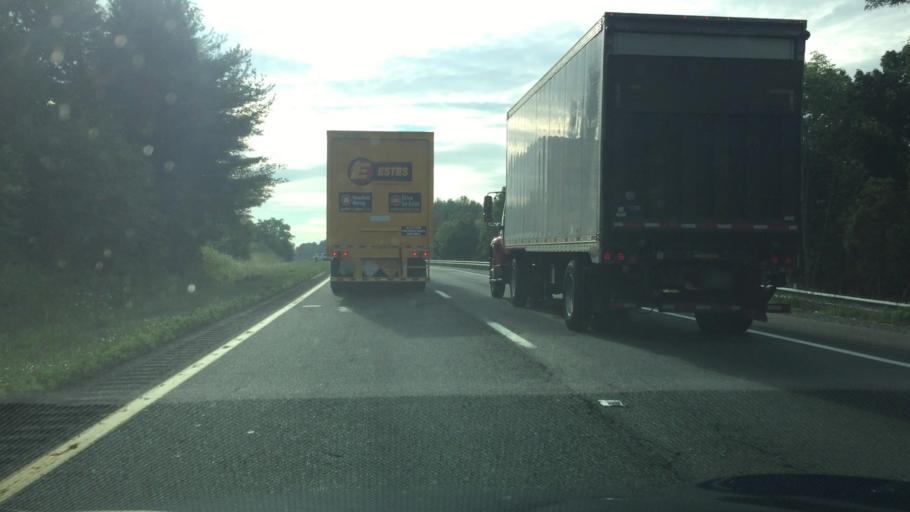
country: US
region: Virginia
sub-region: City of Radford
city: Radford
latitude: 37.0862
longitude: -80.6218
